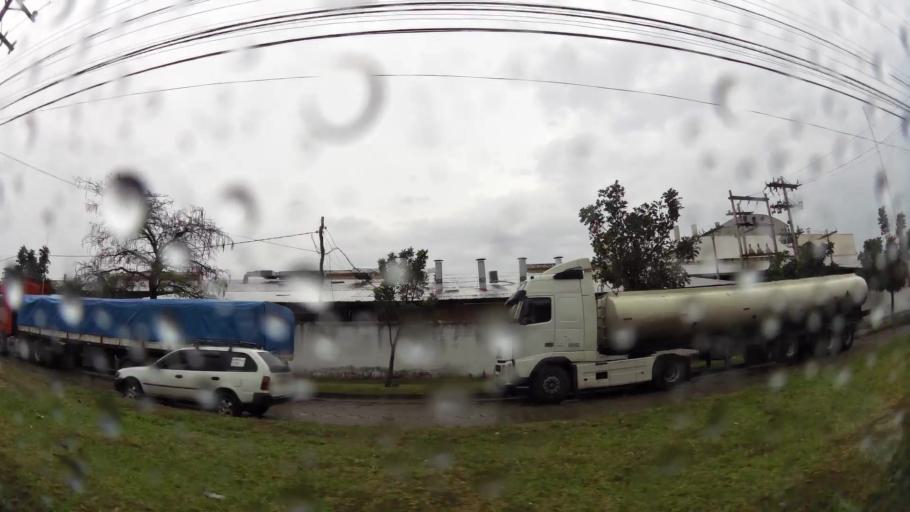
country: BO
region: Santa Cruz
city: Santa Cruz de la Sierra
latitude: -17.7687
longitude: -63.1432
